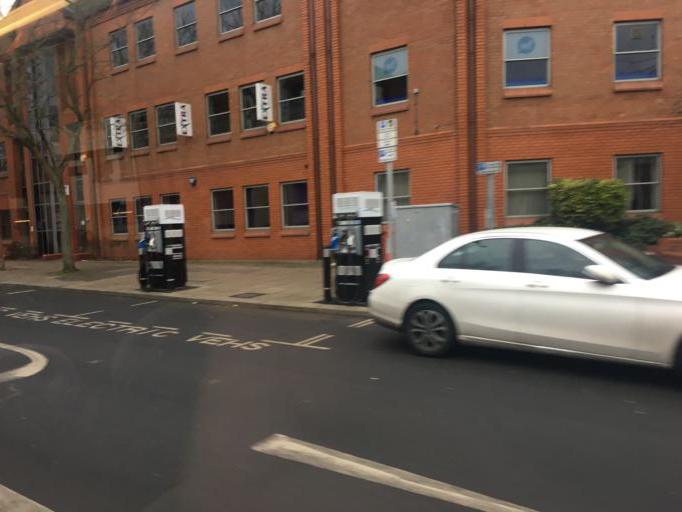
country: GB
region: England
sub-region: Coventry
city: Coventry
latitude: 52.4056
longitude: -1.5156
